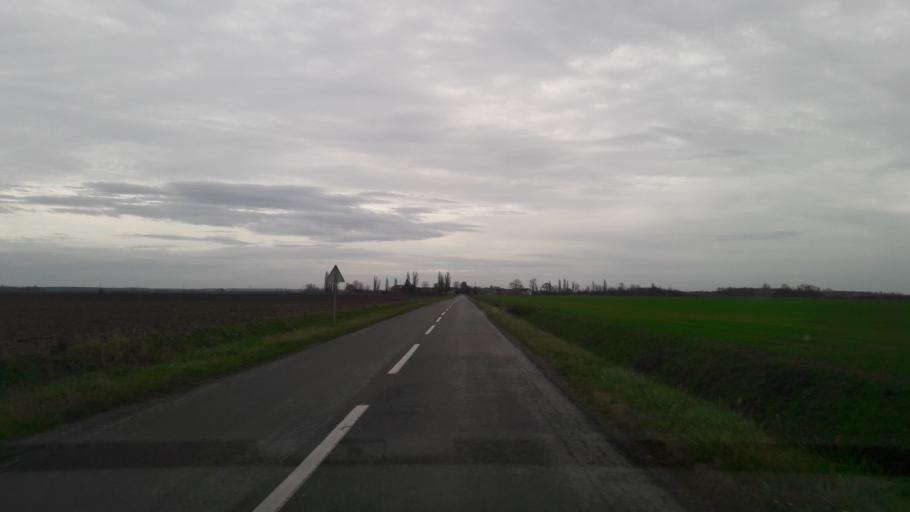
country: HR
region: Virovitick-Podravska
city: Zdenci
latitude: 45.6014
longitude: 17.9899
